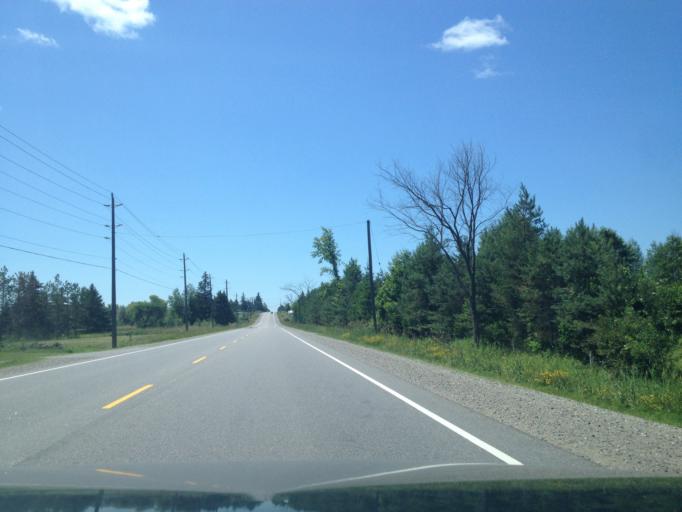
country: CA
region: Ontario
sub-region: Wellington County
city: Guelph
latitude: 43.6240
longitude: -80.0910
